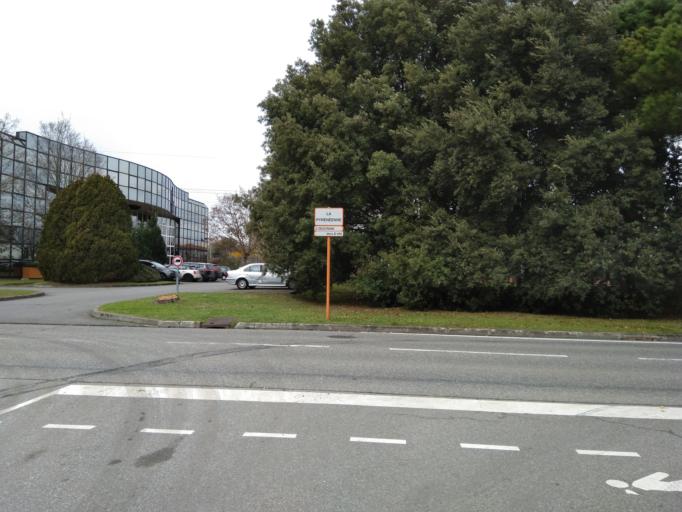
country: FR
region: Midi-Pyrenees
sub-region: Departement de la Haute-Garonne
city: Auzeville-Tolosane
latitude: 43.5448
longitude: 1.5050
